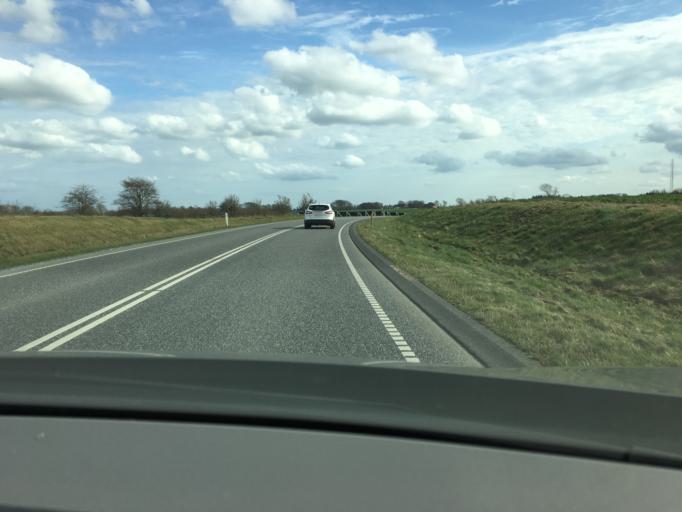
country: DK
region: South Denmark
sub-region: Vejle Kommune
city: Jelling
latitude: 55.7641
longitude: 9.4370
